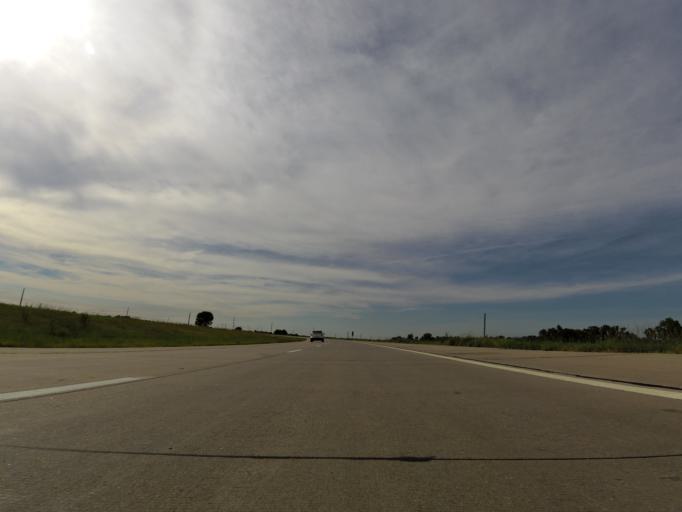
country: US
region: Kansas
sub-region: Sedgwick County
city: Colwich
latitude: 37.8216
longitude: -97.5118
